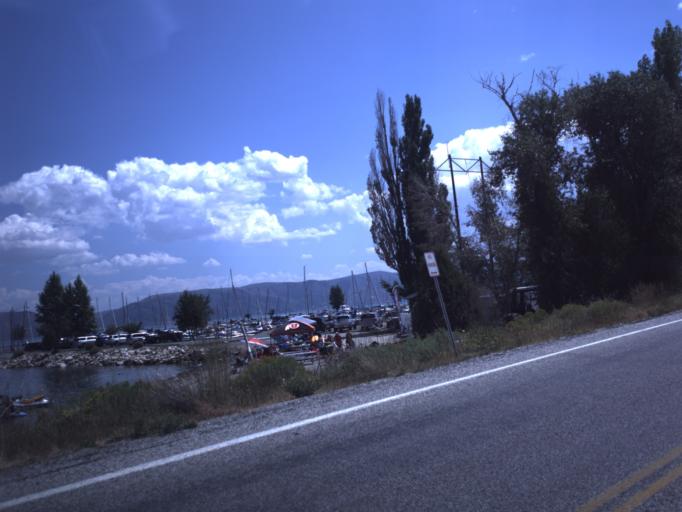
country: US
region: Idaho
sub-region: Bear Lake County
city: Paris
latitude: 41.9667
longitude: -111.3995
